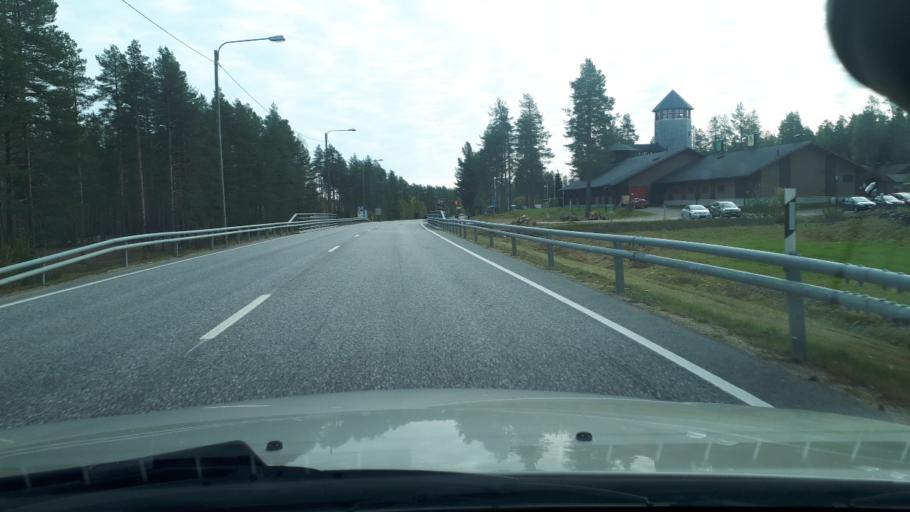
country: FI
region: Lapland
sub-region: Rovaniemi
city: Ranua
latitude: 65.9448
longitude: 26.4645
